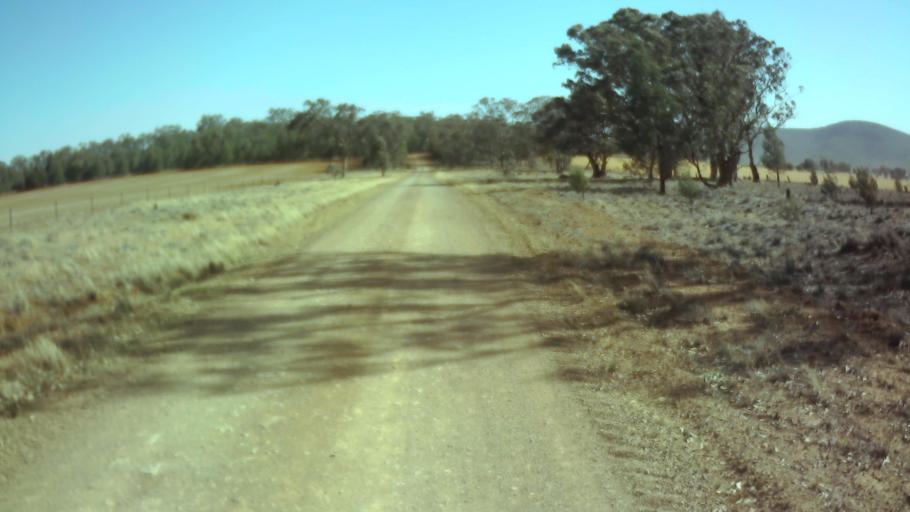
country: AU
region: New South Wales
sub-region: Weddin
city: Grenfell
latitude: -33.8583
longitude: 148.0154
